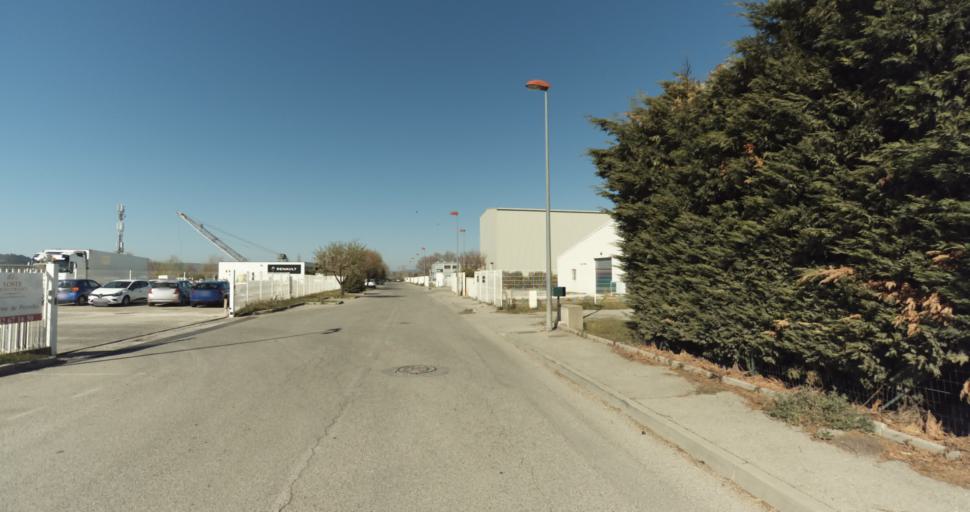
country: FR
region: Provence-Alpes-Cote d'Azur
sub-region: Departement des Bouches-du-Rhone
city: Peyrolles-en-Provence
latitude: 43.6561
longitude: 5.5788
